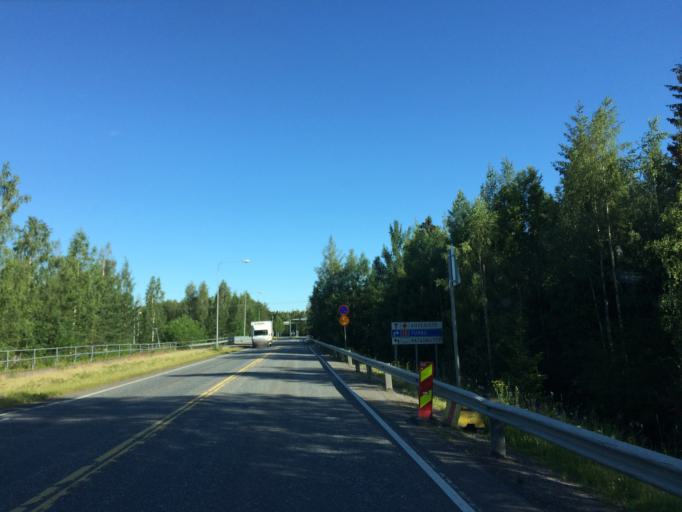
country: FI
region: Haeme
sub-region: Haemeenlinna
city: Haemeenlinna
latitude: 60.9634
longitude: 24.4503
